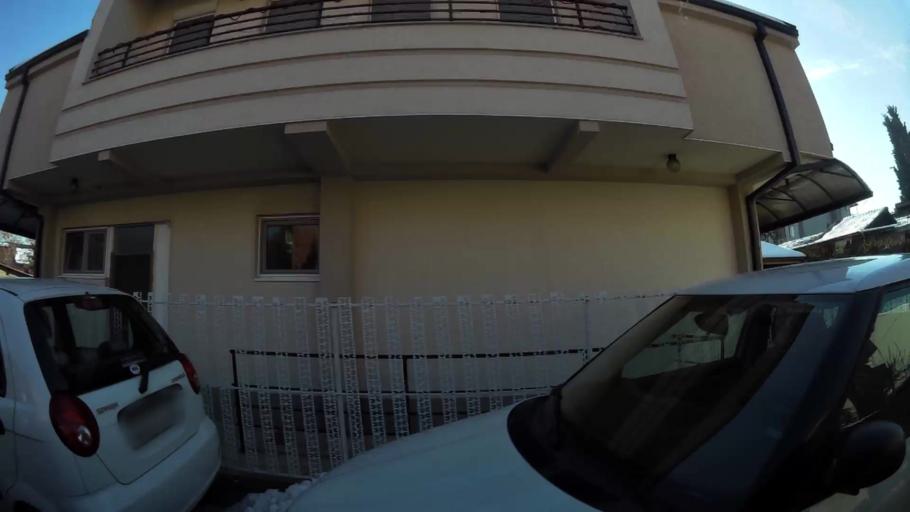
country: MK
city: Krushopek
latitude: 42.0085
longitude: 21.3757
